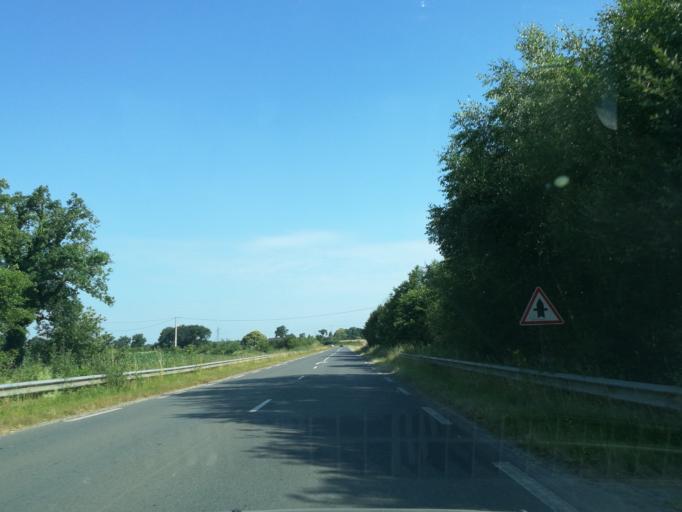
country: FR
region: Brittany
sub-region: Departement d'Ille-et-Vilaine
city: Montfort-sur-Meu
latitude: 48.1437
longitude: -1.9399
